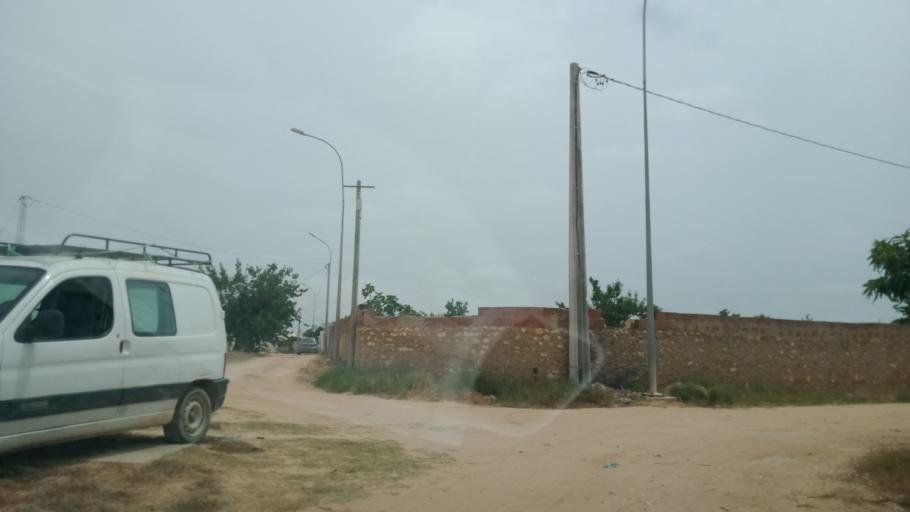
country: TN
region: Safaqis
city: Al Qarmadah
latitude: 34.8119
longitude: 10.7447
